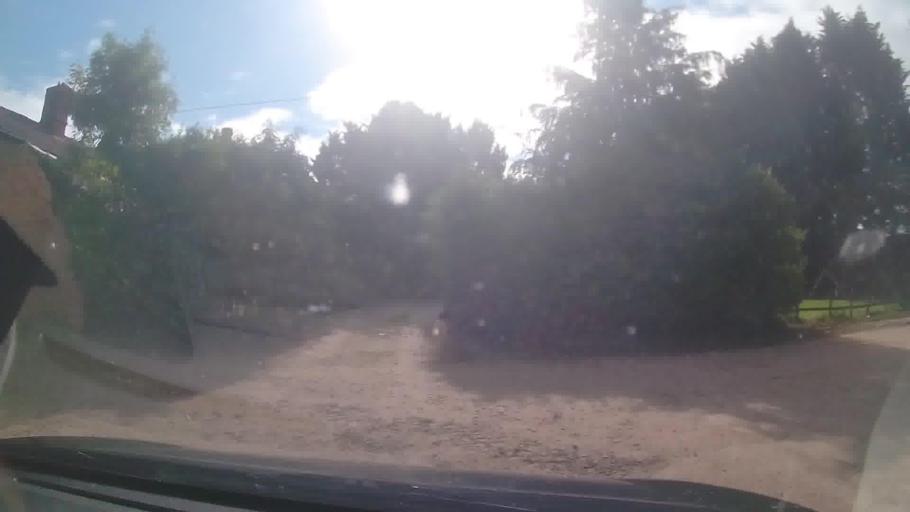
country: GB
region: England
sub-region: Shropshire
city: Prees
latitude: 52.8736
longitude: -2.6320
